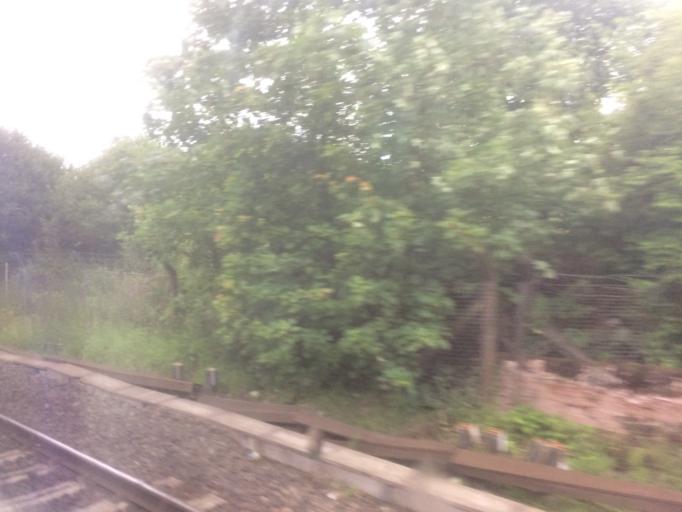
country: GB
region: Scotland
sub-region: Glasgow City
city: Glasgow
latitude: 55.8758
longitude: -4.2425
